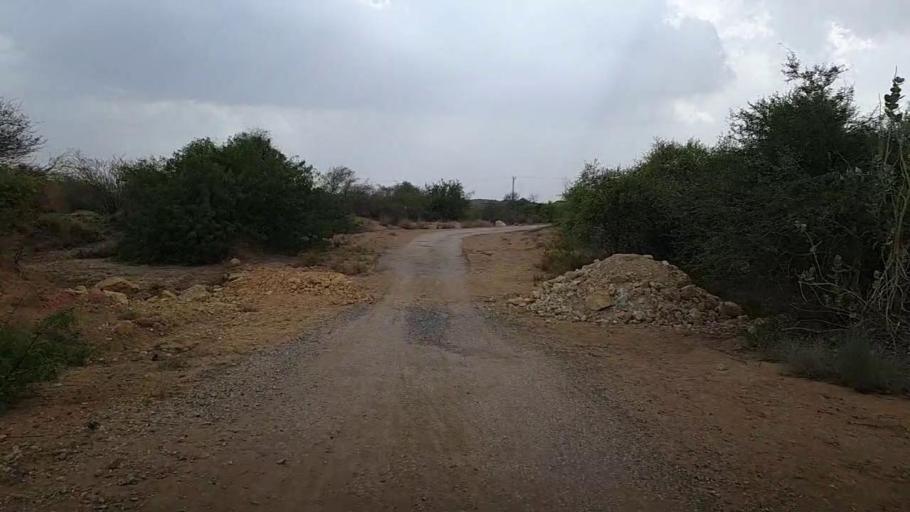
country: PK
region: Sindh
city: Jamshoro
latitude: 25.3935
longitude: 67.6891
